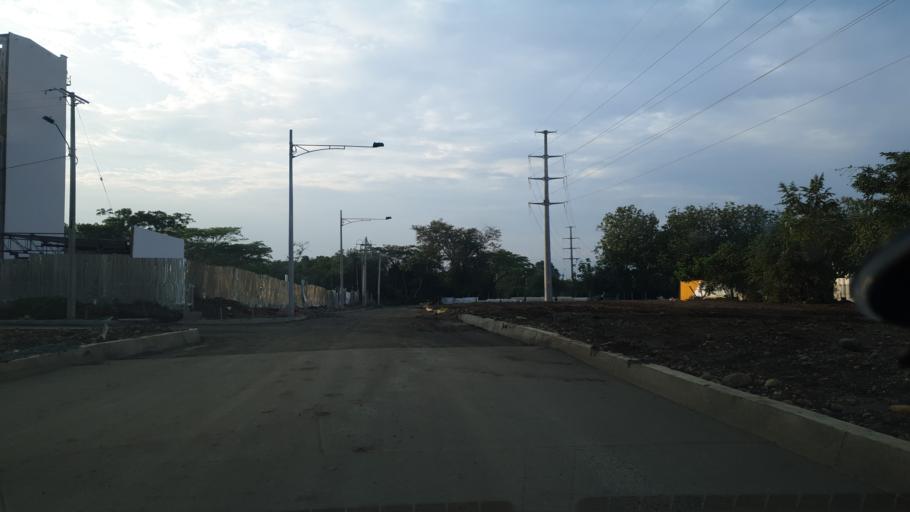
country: CO
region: Valle del Cauca
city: Jamundi
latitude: 3.3466
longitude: -76.5154
